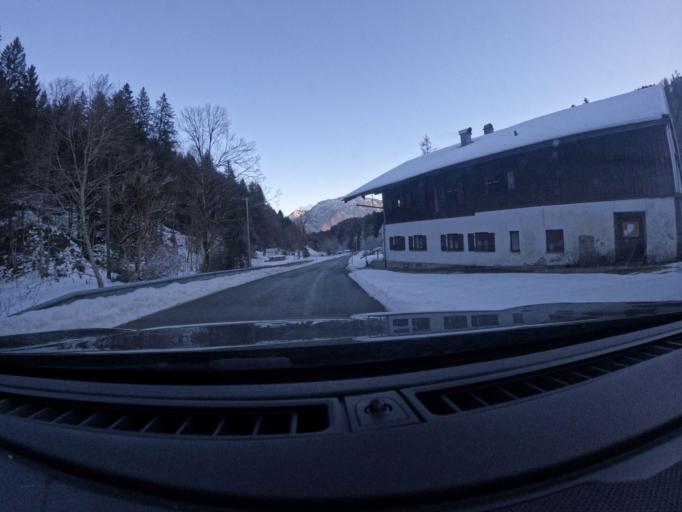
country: DE
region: Bavaria
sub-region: Upper Bavaria
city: Ruhpolding
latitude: 47.7617
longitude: 12.6127
